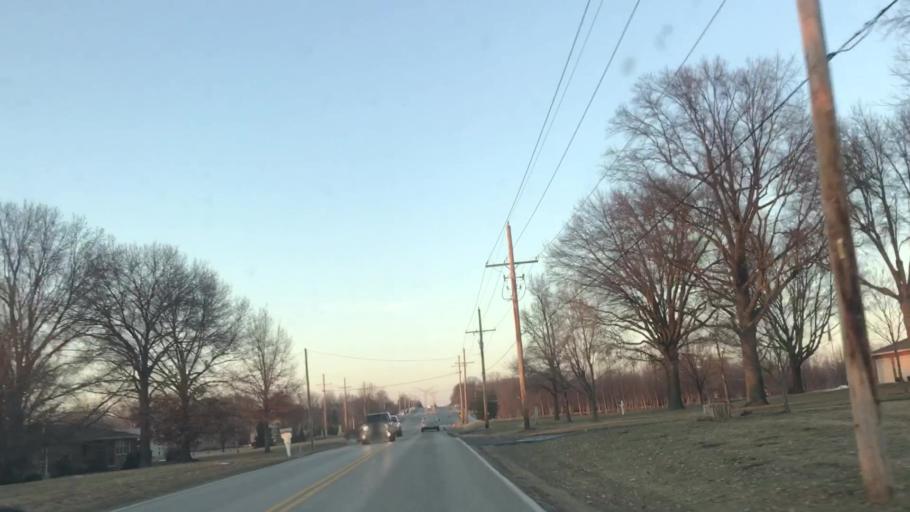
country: US
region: Kansas
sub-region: Johnson County
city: Lenexa
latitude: 38.8361
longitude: -94.7052
